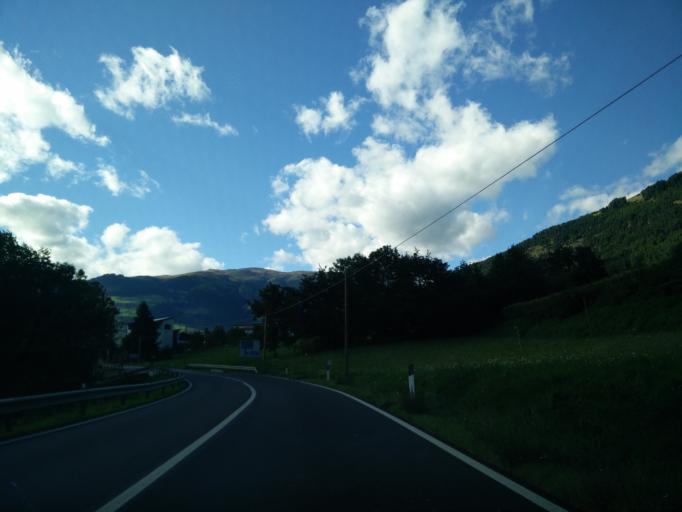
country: IT
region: Trentino-Alto Adige
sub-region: Bolzano
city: Glorenza
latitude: 46.6795
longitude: 10.5666
